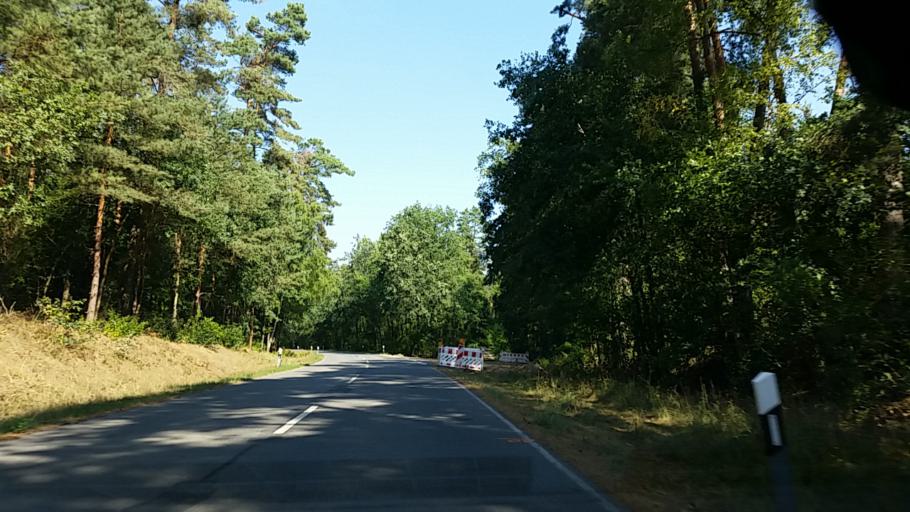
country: DE
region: Lower Saxony
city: Jelmstorf
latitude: 53.1126
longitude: 10.5476
